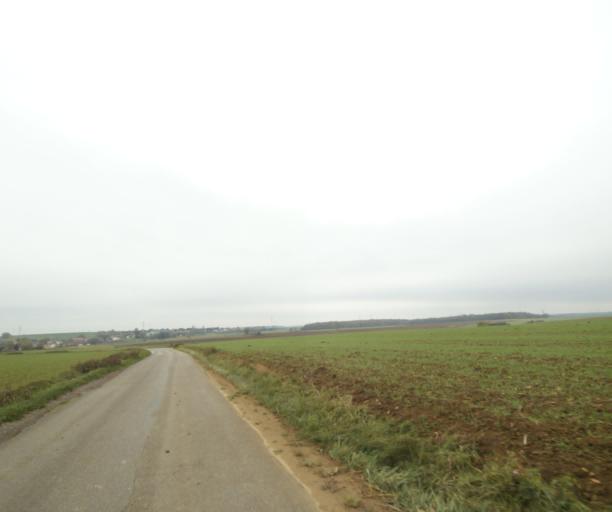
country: FR
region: Lorraine
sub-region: Departement de Meurthe-et-Moselle
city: Briey
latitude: 49.2579
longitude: 5.9103
